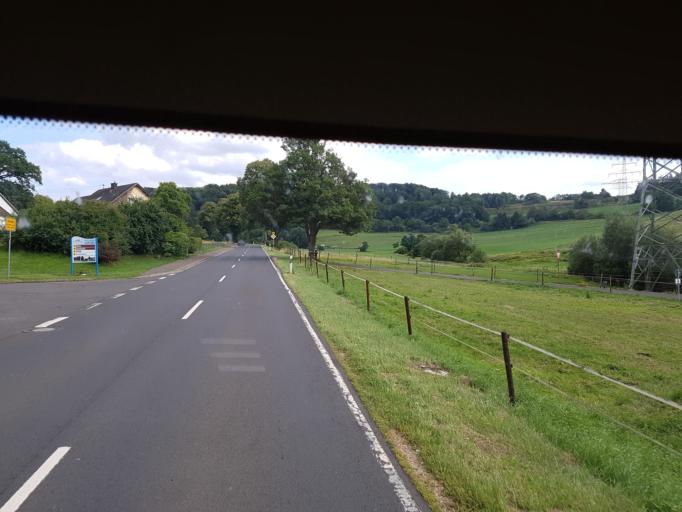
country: DE
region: Rheinland-Pfalz
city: Hohenfels-Essingen
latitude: 50.2537
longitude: 6.7264
